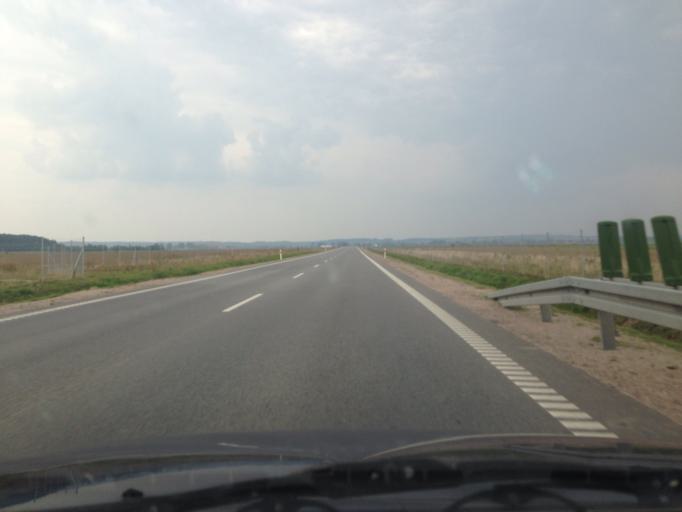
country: PL
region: Pomeranian Voivodeship
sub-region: Powiat kwidzynski
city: Kwidzyn
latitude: 53.7554
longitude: 18.8958
